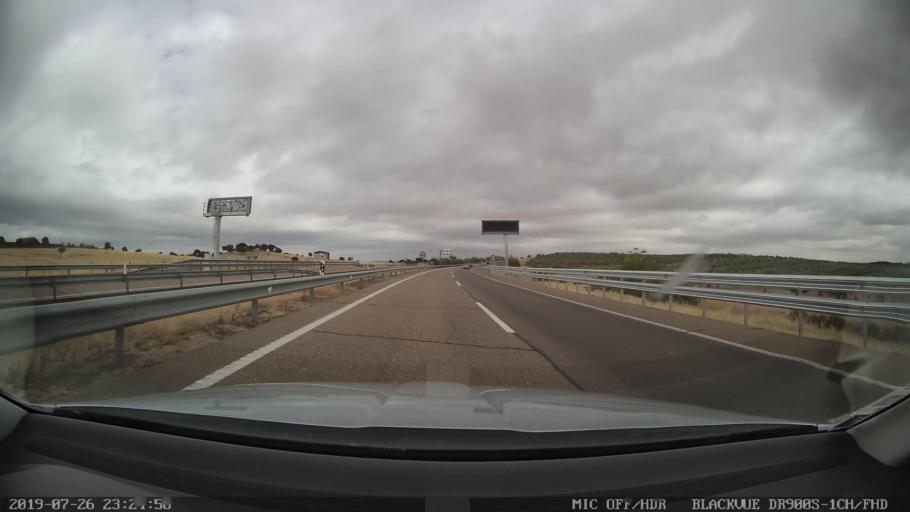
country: ES
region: Extremadura
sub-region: Provincia de Caceres
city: Escurial
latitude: 39.1815
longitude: -5.8966
